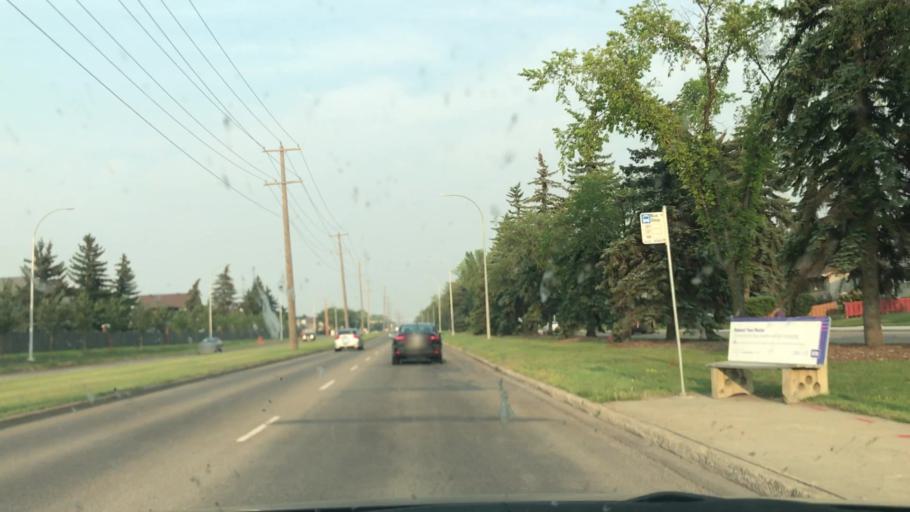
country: CA
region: Alberta
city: Edmonton
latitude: 53.5994
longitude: -113.5118
